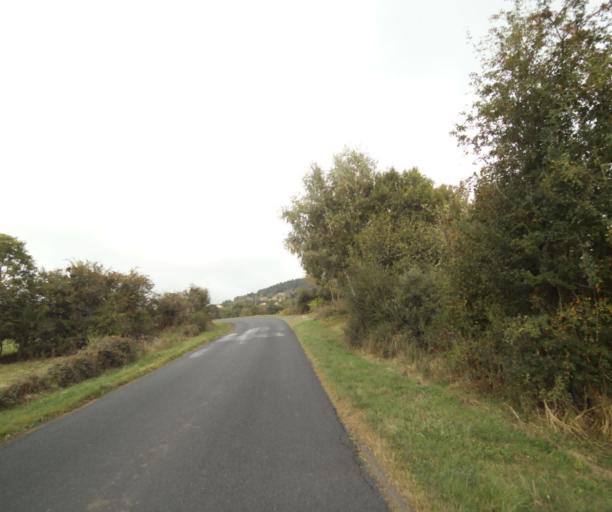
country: FR
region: Auvergne
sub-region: Departement du Puy-de-Dome
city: Saint-Genes-Champanelle
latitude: 45.7103
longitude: 3.0002
